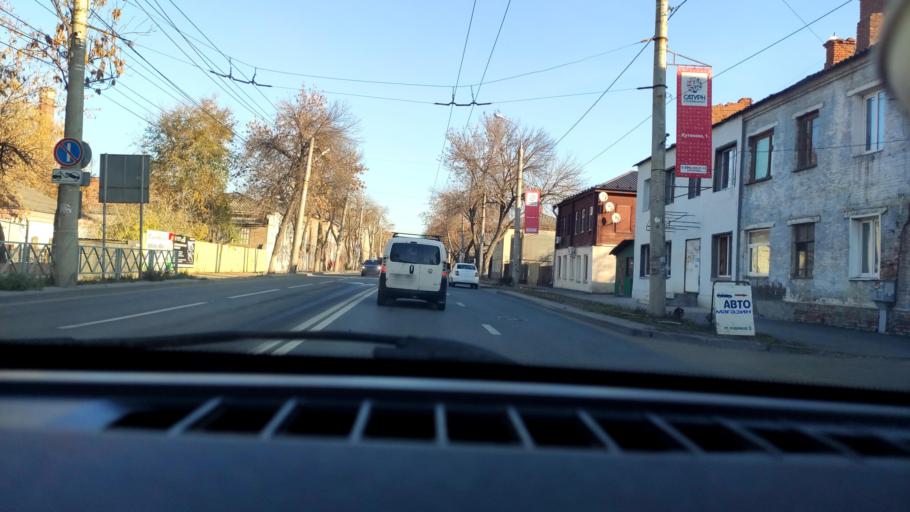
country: RU
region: Samara
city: Rozhdestveno
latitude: 53.1780
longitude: 50.0752
